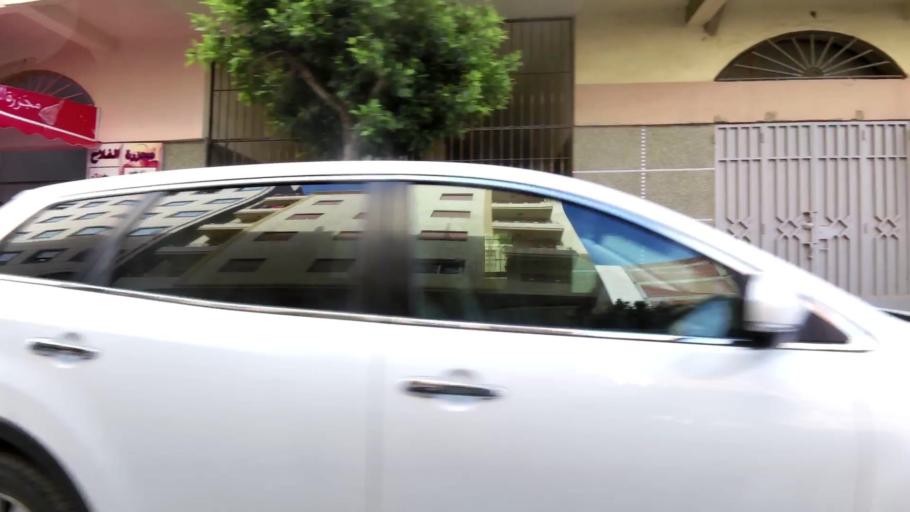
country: MA
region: Tanger-Tetouan
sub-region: Tanger-Assilah
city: Tangier
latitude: 35.7425
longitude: -5.7974
